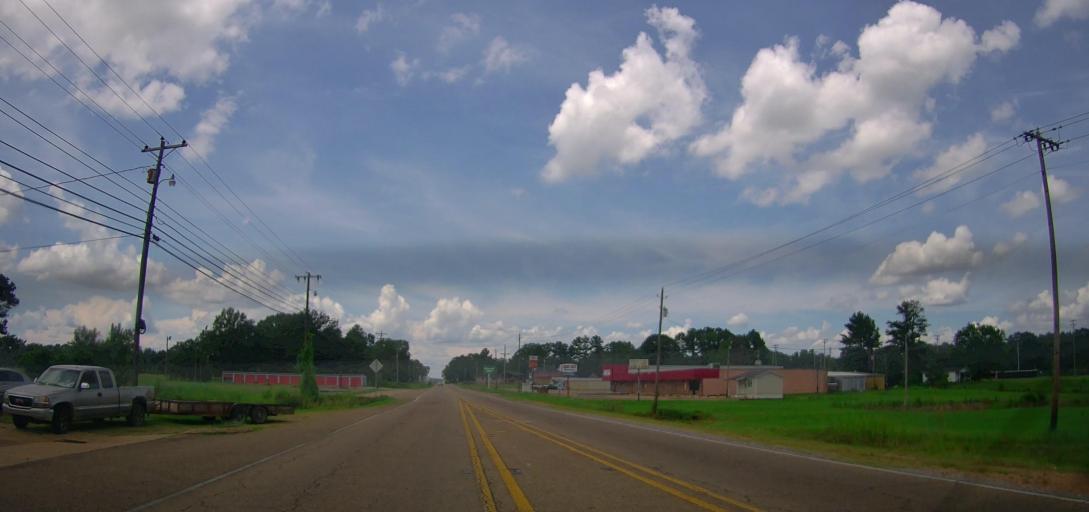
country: US
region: Mississippi
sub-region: Lee County
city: Shannon
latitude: 34.1268
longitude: -88.7193
